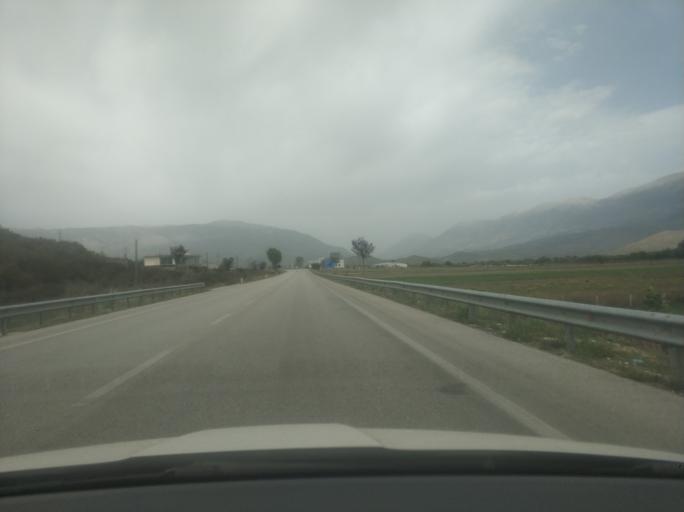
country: AL
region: Gjirokaster
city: Gjirokaster
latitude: 40.1144
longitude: 20.1194
